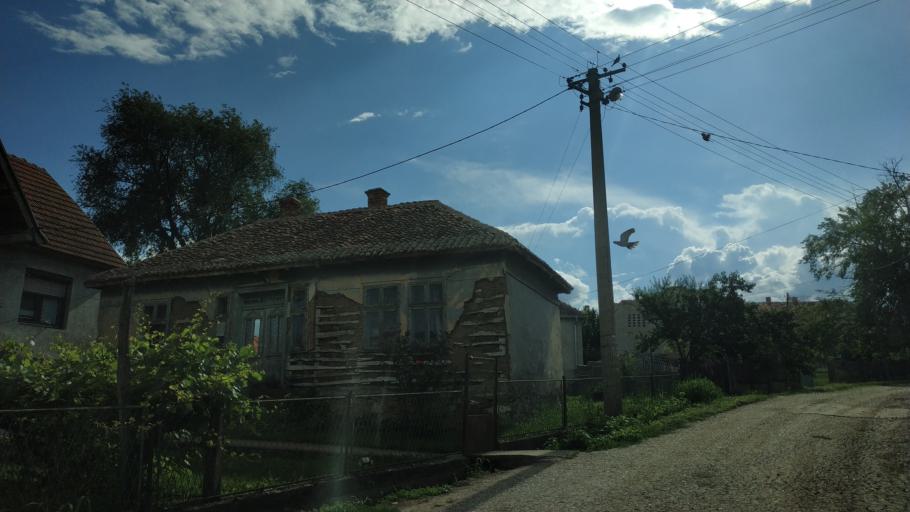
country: RS
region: Central Serbia
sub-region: Nisavski Okrug
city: Aleksinac
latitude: 43.6196
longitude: 21.6448
